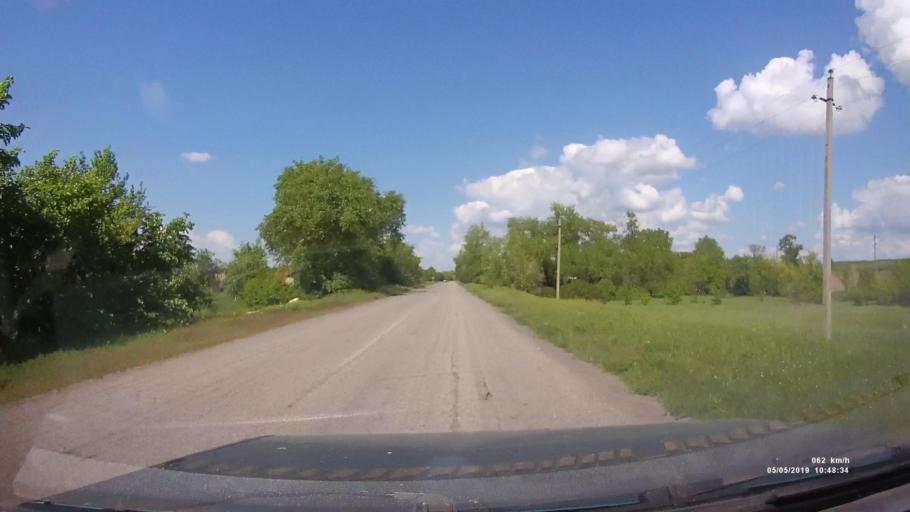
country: RU
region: Rostov
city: Ust'-Donetskiy
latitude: 47.6432
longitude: 40.8184
